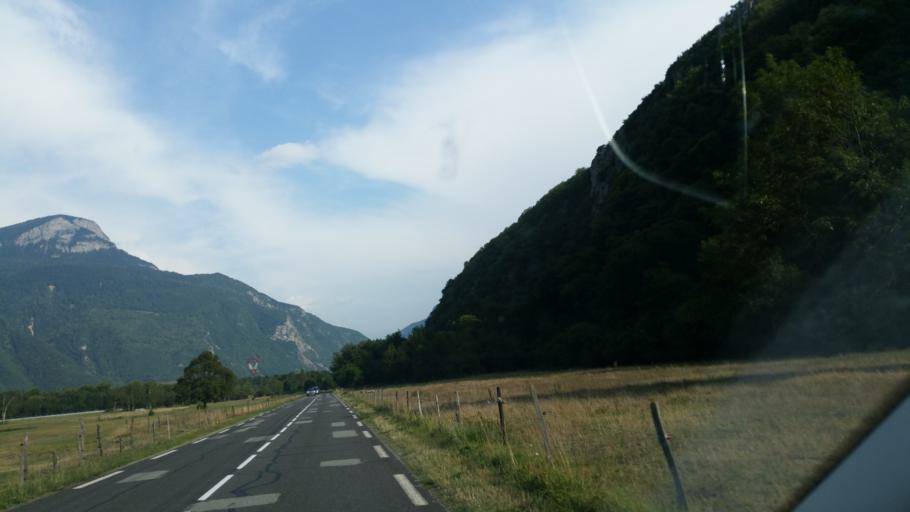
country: FR
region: Rhone-Alpes
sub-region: Departement de la Savoie
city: Saint-Etienne-de-Cuines
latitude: 45.3681
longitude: 6.2797
